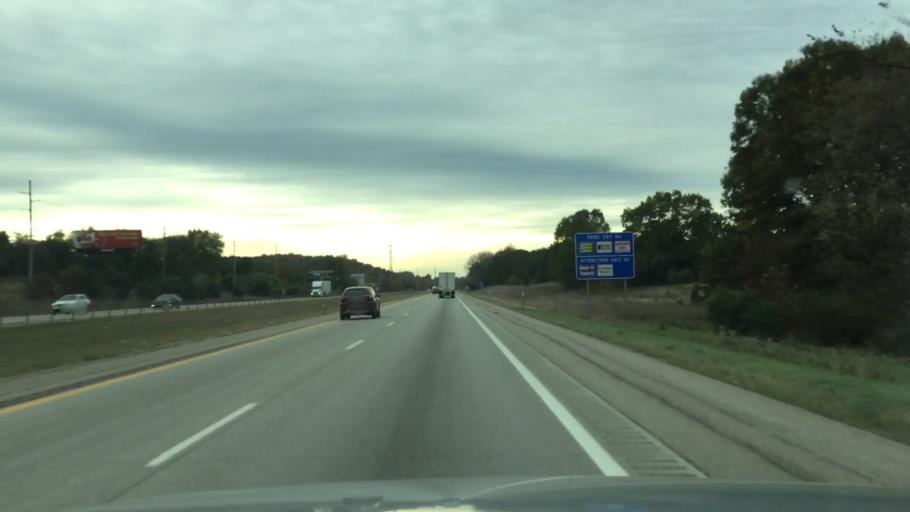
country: US
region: Michigan
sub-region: Van Buren County
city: Paw Paw
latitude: 42.2113
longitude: -85.8710
